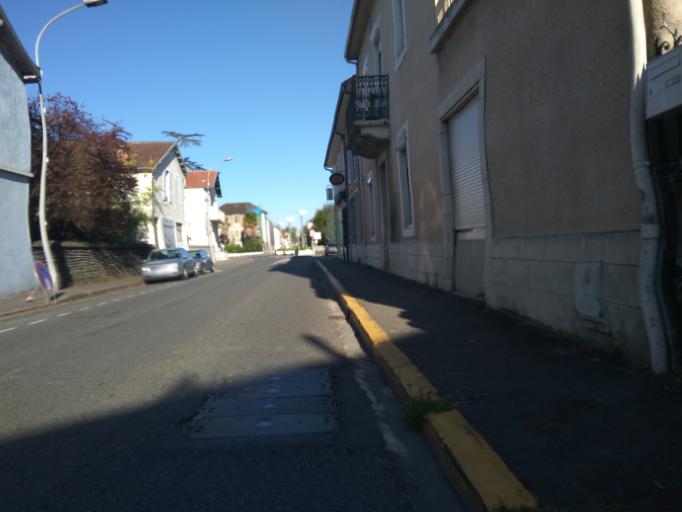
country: FR
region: Aquitaine
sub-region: Departement des Pyrenees-Atlantiques
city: Bizanos
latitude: 43.2877
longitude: -0.3518
